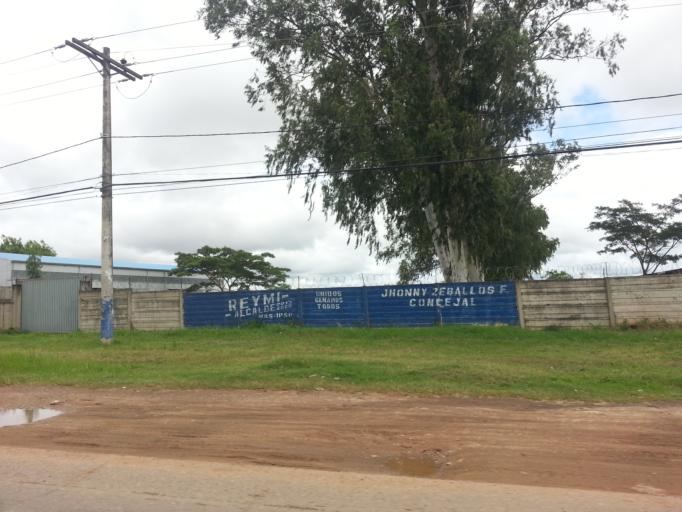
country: BO
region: Santa Cruz
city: Santa Cruz de la Sierra
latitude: -17.7111
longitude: -63.1605
